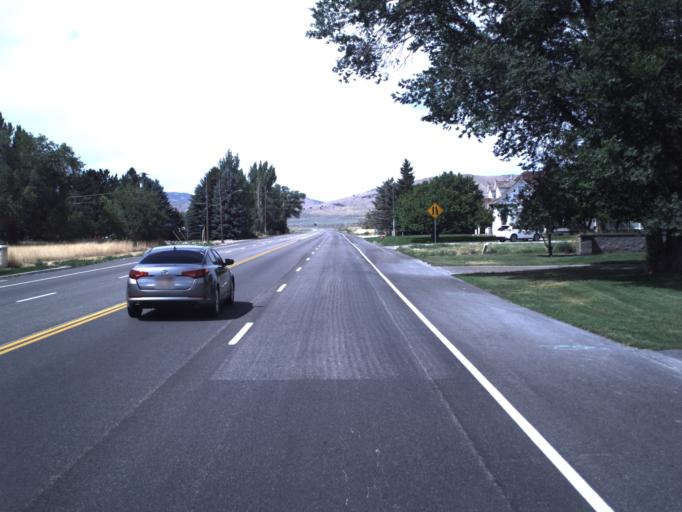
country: US
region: Utah
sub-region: Sanpete County
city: Fountain Green
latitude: 39.6342
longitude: -111.6344
